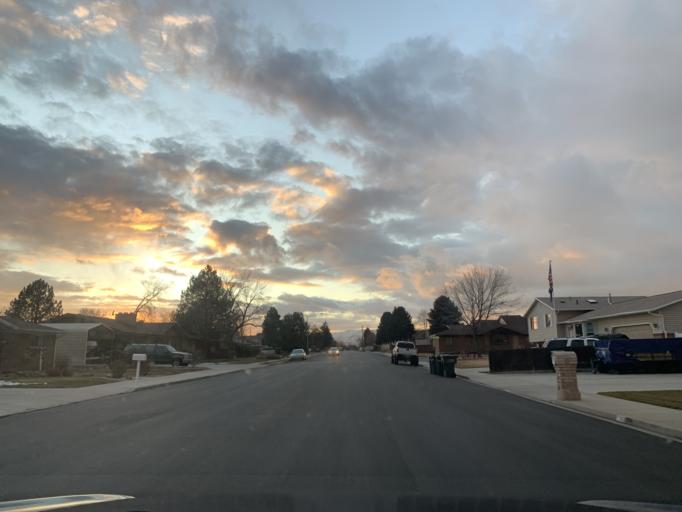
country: US
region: Utah
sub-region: Utah County
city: Provo
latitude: 40.2565
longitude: -111.6782
